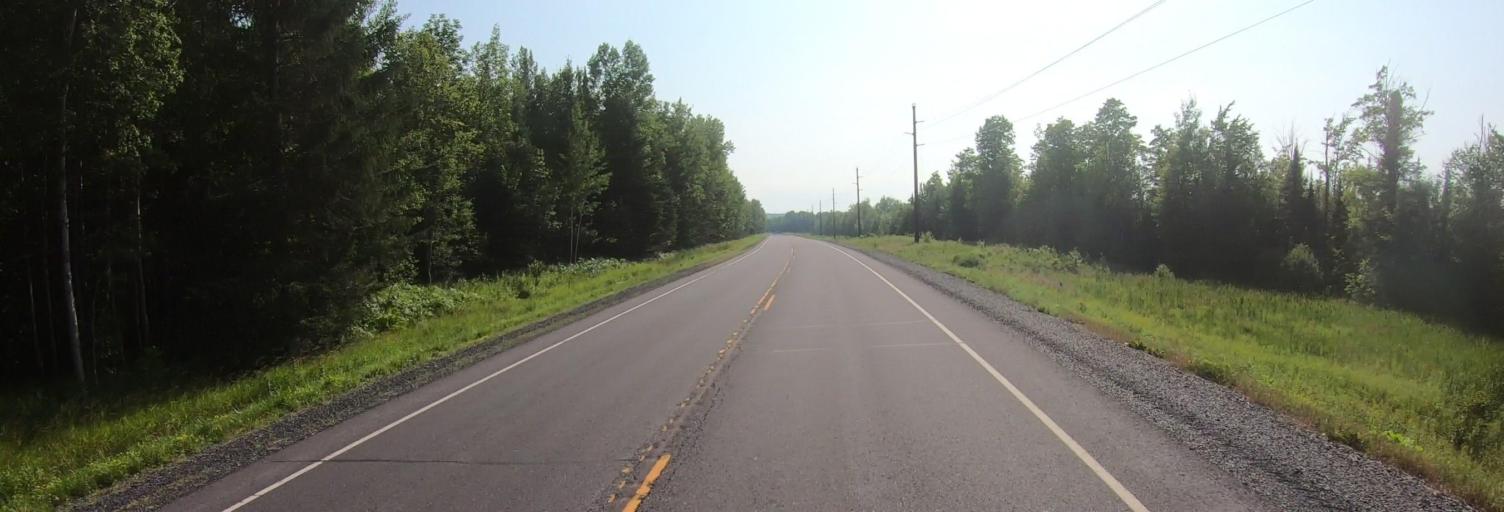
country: US
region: Wisconsin
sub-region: Iron County
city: Hurley
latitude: 46.3752
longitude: -90.3881
